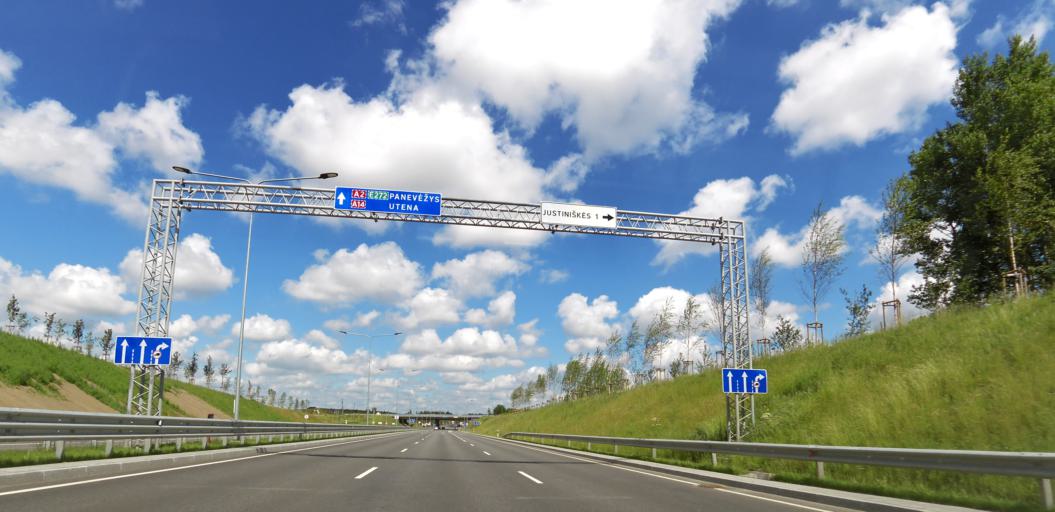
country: LT
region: Vilnius County
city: Justiniskes
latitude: 54.7218
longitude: 25.2082
